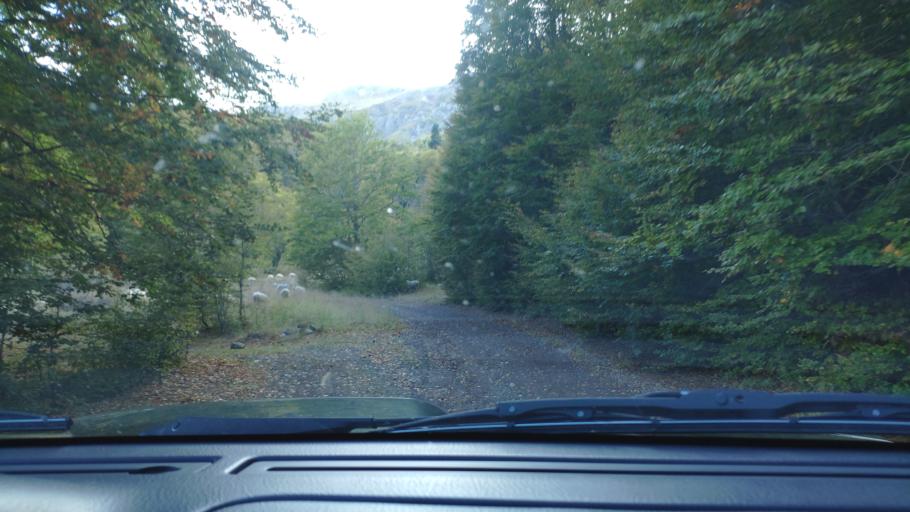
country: GR
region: West Macedonia
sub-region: Nomos Kastorias
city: Nestorio
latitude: 40.3241
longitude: 20.9060
